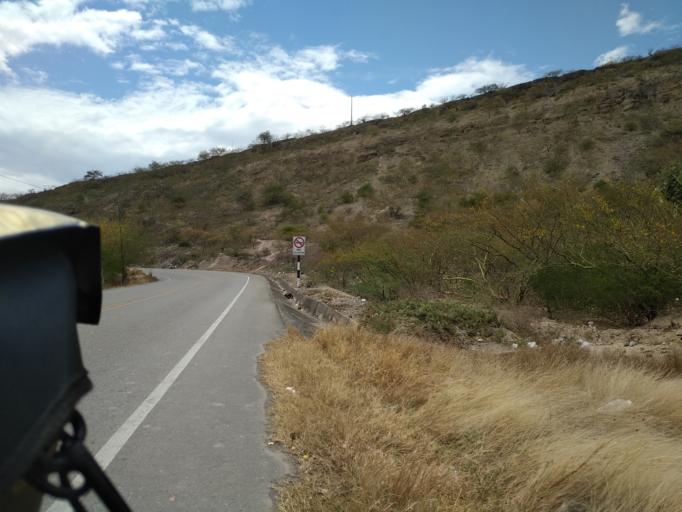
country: PE
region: Cajamarca
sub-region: Provincia de Jaen
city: Bellavista
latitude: -5.7432
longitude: -78.6582
